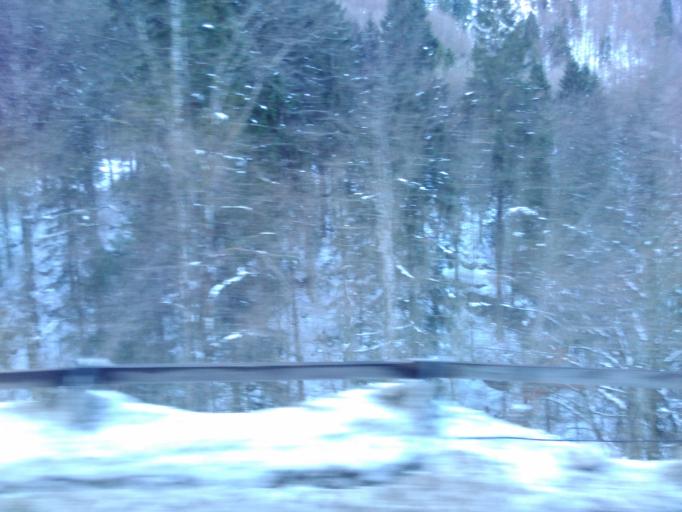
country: CH
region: Schwyz
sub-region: Bezirk March
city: Vorderthal
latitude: 47.1122
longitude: 8.8994
